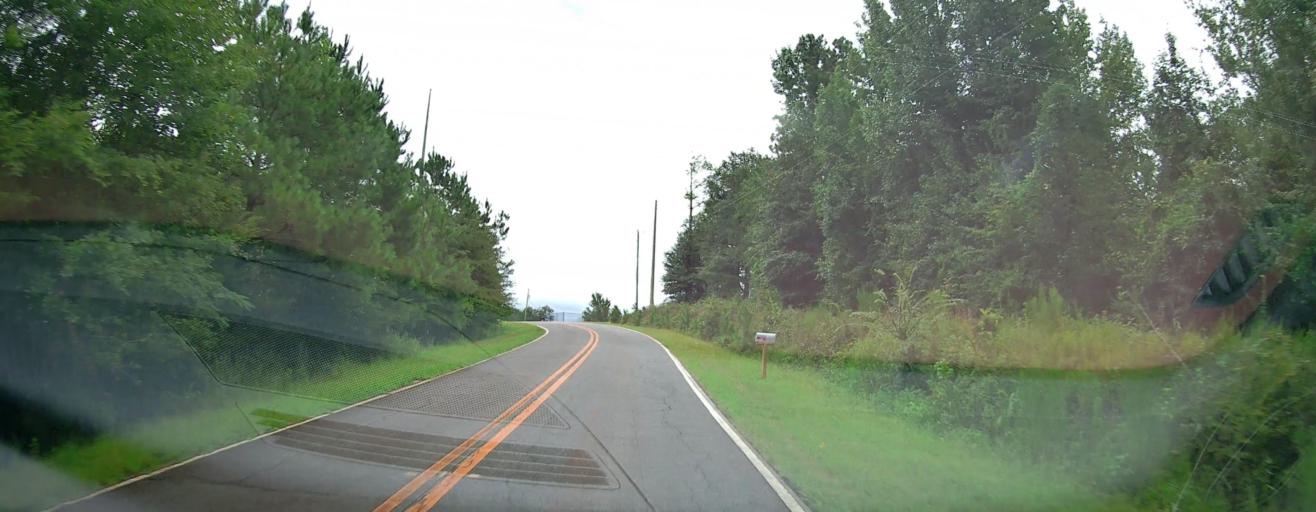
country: US
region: Georgia
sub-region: Bibb County
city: Macon
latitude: 32.7932
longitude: -83.5234
